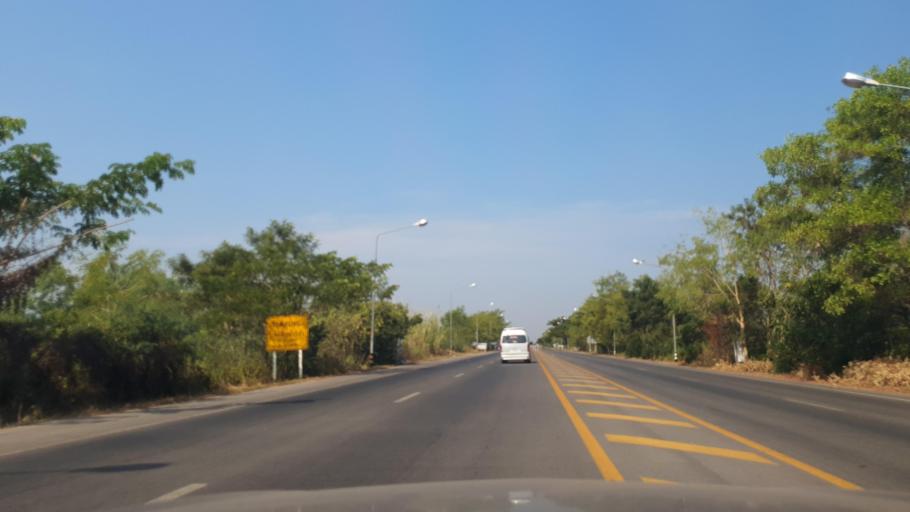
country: TH
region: Nakhon Phanom
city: Ban Phaeng
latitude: 17.9480
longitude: 104.2221
